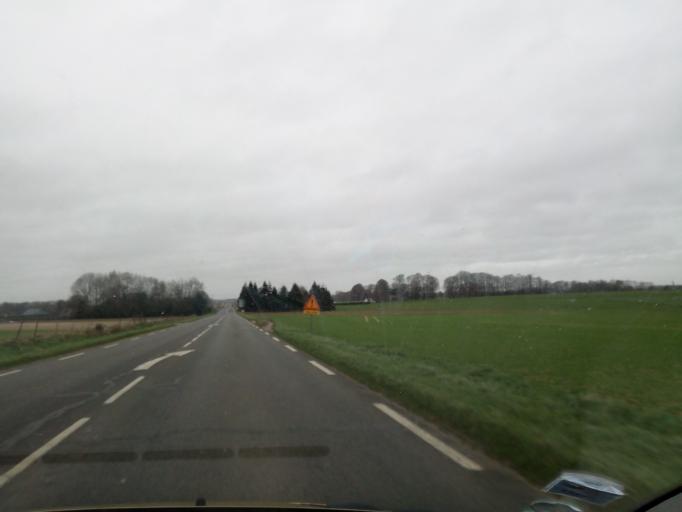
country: FR
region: Haute-Normandie
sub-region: Departement de la Seine-Maritime
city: Auzebosc
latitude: 49.5810
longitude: 0.7303
